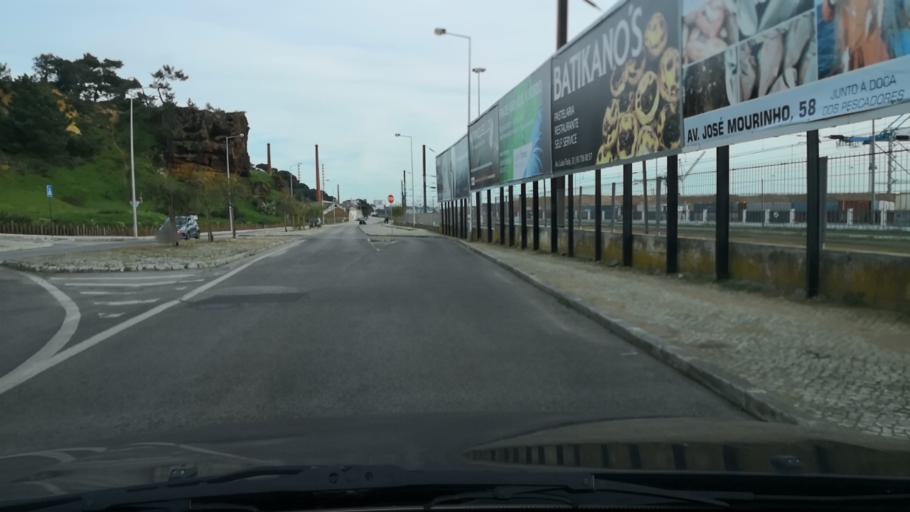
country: PT
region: Setubal
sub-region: Setubal
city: Setubal
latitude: 38.5197
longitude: -8.8777
